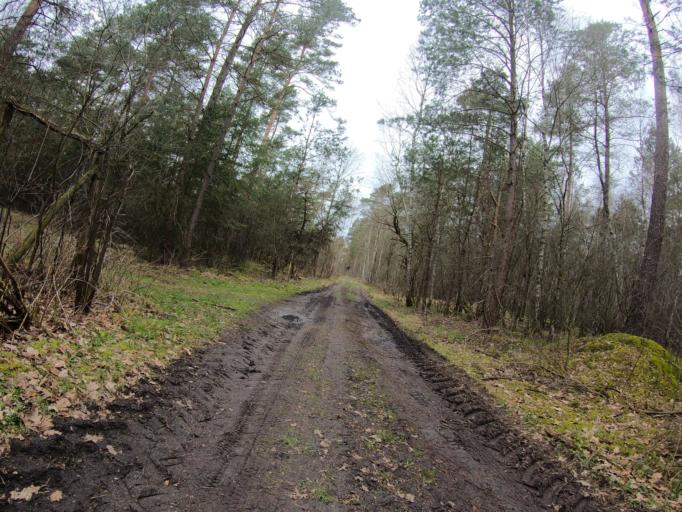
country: DE
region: Lower Saxony
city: Leiferde
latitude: 52.4870
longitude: 10.4470
